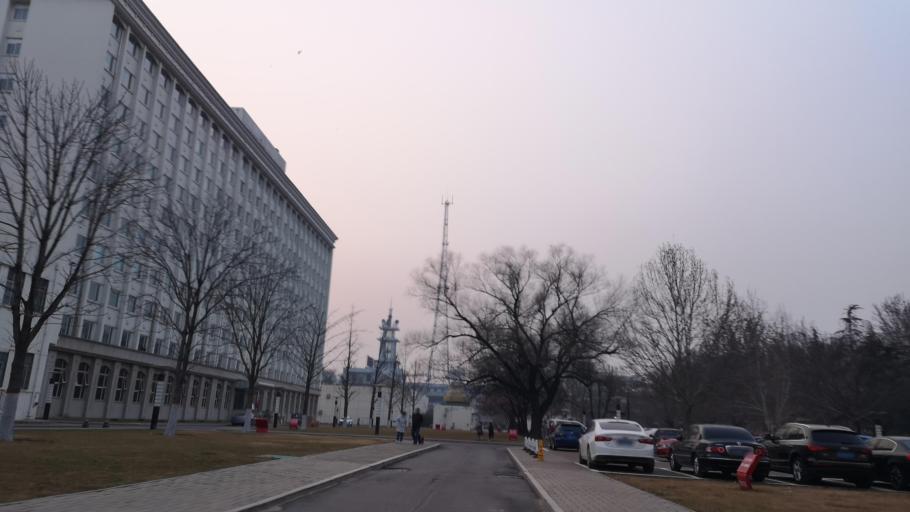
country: CN
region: Henan Sheng
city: Zhongyuanlu
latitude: 35.7771
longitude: 115.0750
